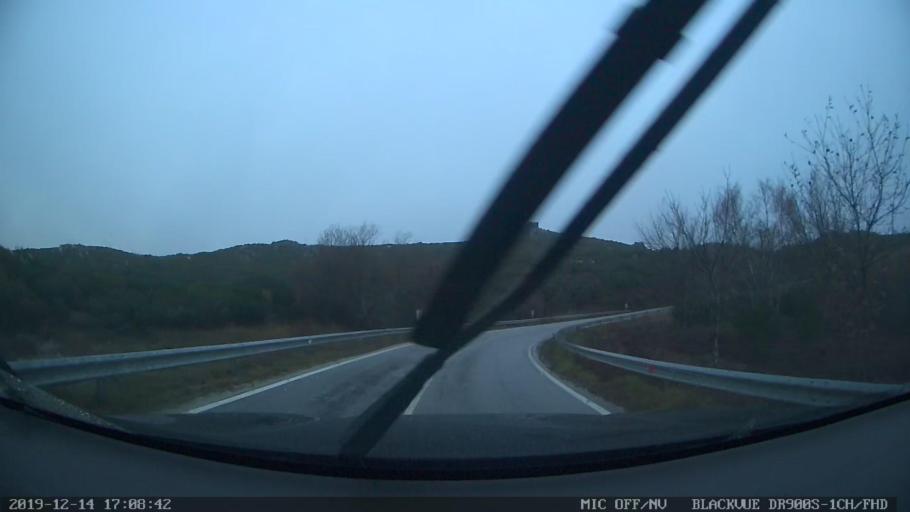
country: PT
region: Vila Real
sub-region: Vila Pouca de Aguiar
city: Vila Pouca de Aguiar
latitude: 41.4709
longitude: -7.6042
